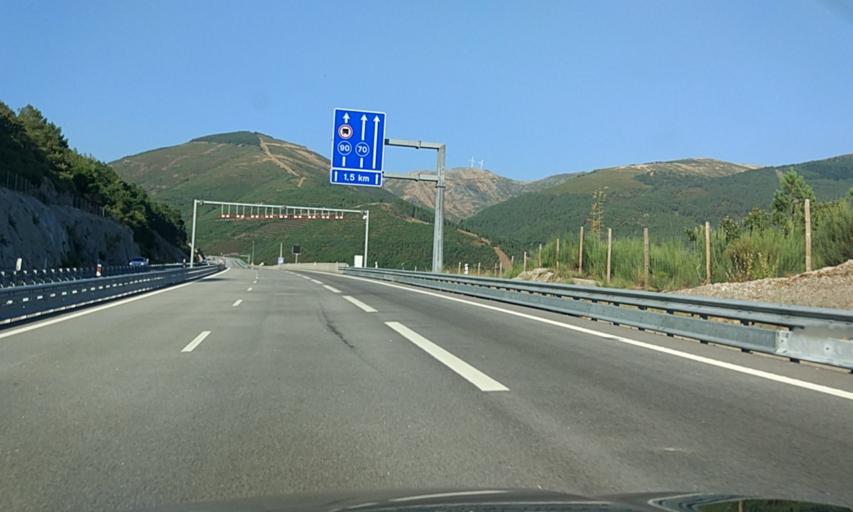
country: PT
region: Porto
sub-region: Baiao
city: Valadares
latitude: 41.2541
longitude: -7.9585
